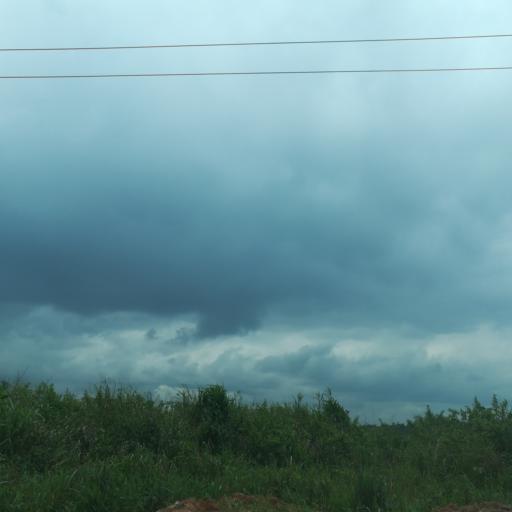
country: NG
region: Lagos
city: Ejirin
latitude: 6.6465
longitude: 3.8401
